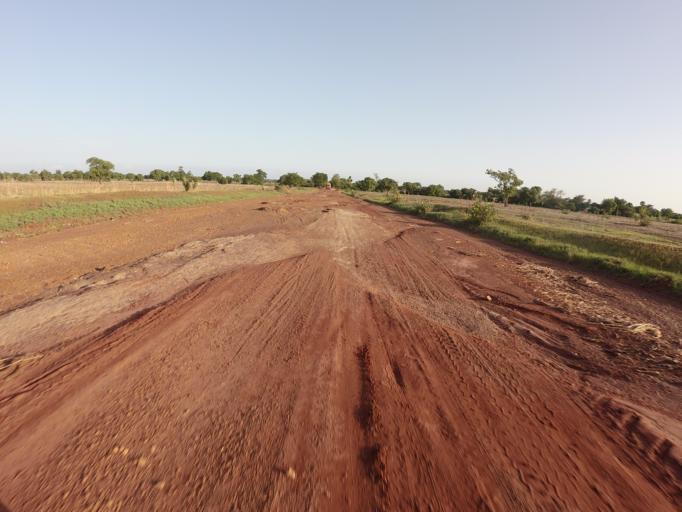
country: TG
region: Savanes
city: Sansanne-Mango
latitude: 10.3504
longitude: -0.0929
